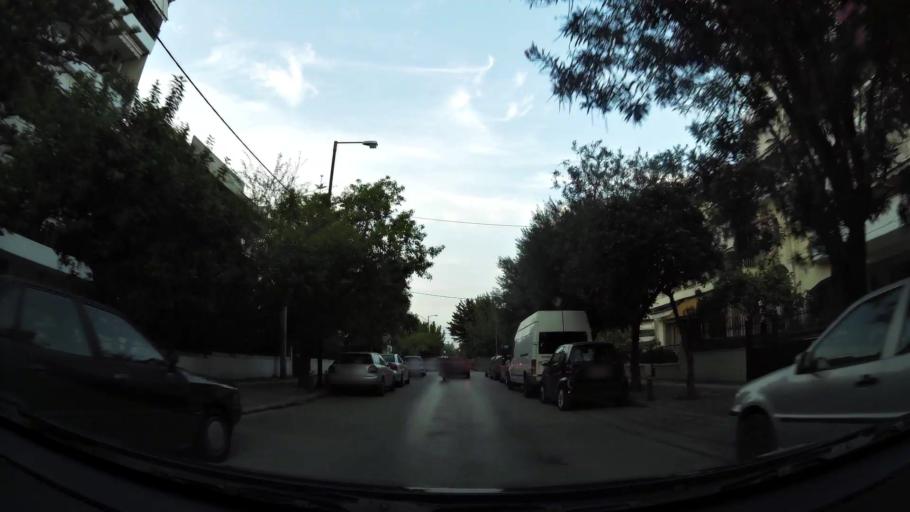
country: GR
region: Attica
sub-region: Nomarchia Athinas
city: Moskhaton
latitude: 37.9475
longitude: 23.6761
